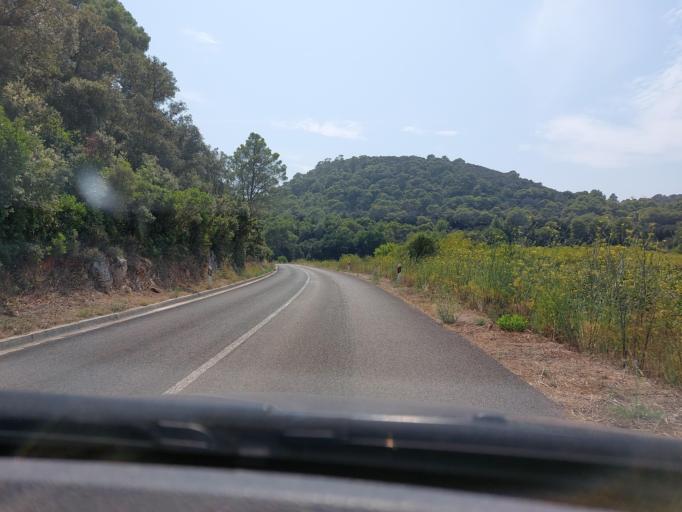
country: HR
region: Dubrovacko-Neretvanska
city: Smokvica
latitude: 42.7535
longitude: 16.8374
